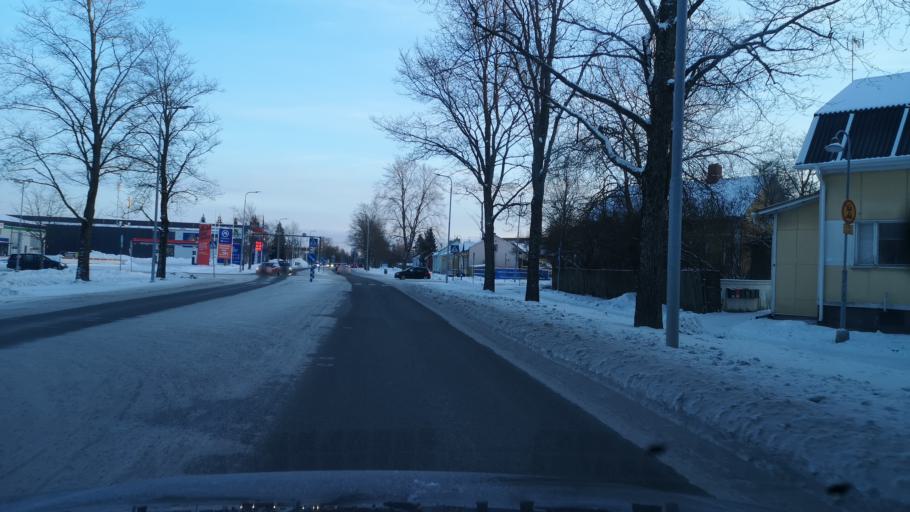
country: FI
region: Satakunta
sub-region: Pori
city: Pori
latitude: 61.4847
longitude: 21.8092
